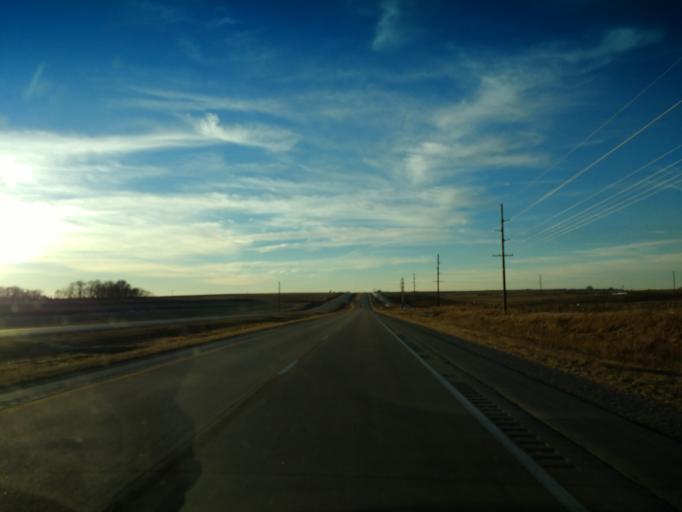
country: US
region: Iowa
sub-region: Ida County
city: Holstein
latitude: 42.4751
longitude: -95.4905
